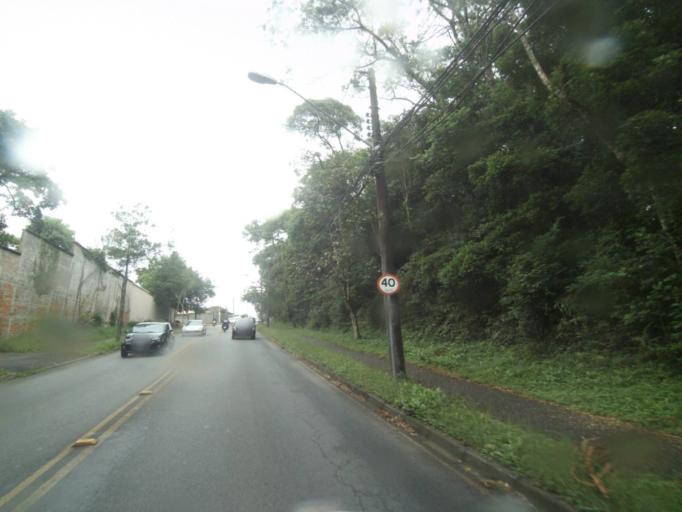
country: BR
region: Parana
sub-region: Curitiba
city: Curitiba
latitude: -25.4228
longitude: -49.3147
